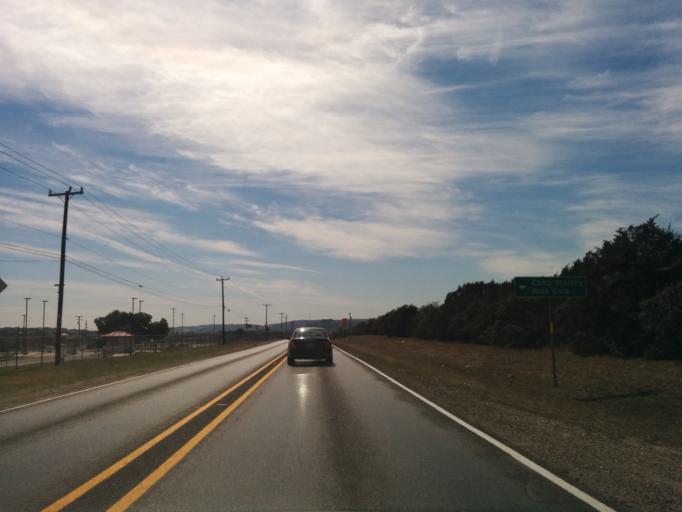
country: US
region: Texas
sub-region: Bexar County
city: Cross Mountain
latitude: 29.6867
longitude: -98.6315
